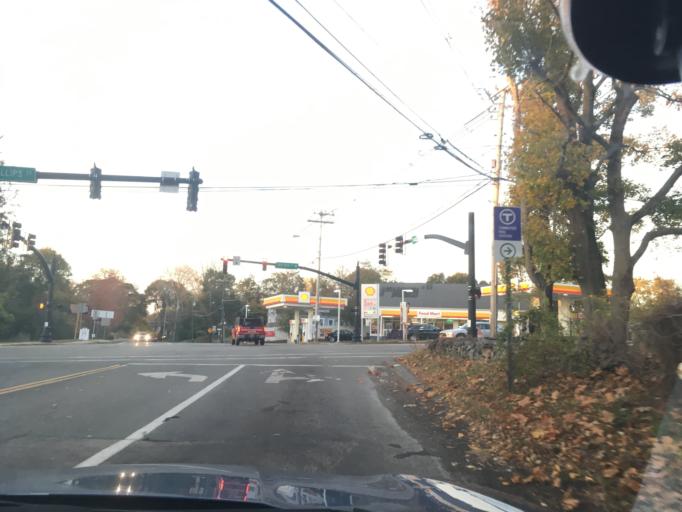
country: US
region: Rhode Island
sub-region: Washington County
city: North Kingstown
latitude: 41.5666
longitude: -71.4636
